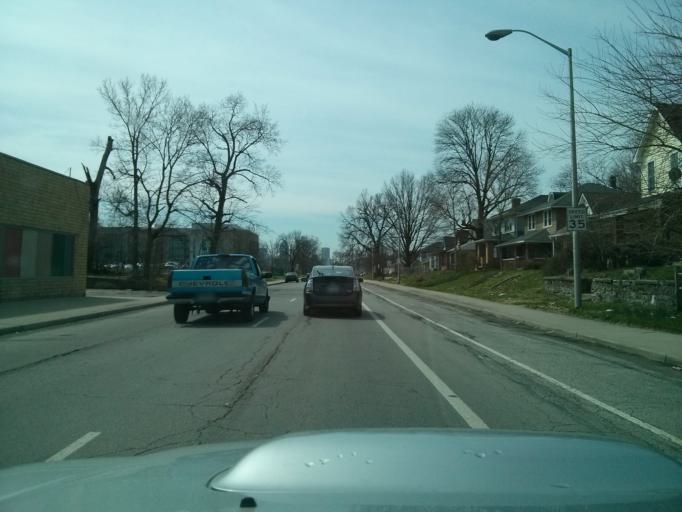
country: US
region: Indiana
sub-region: Marion County
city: Indianapolis
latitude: 39.8064
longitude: -86.1614
